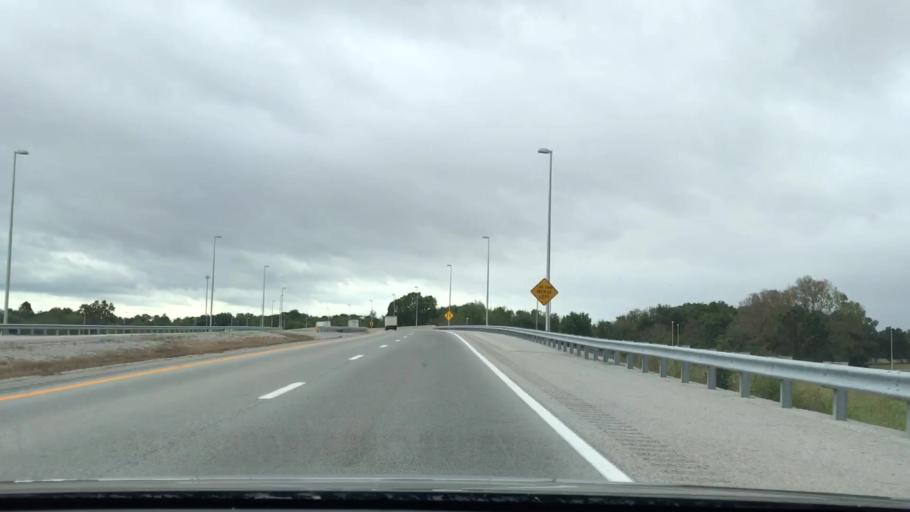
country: US
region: Kentucky
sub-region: Christian County
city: Fort Campbell North
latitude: 36.7460
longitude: -87.5106
